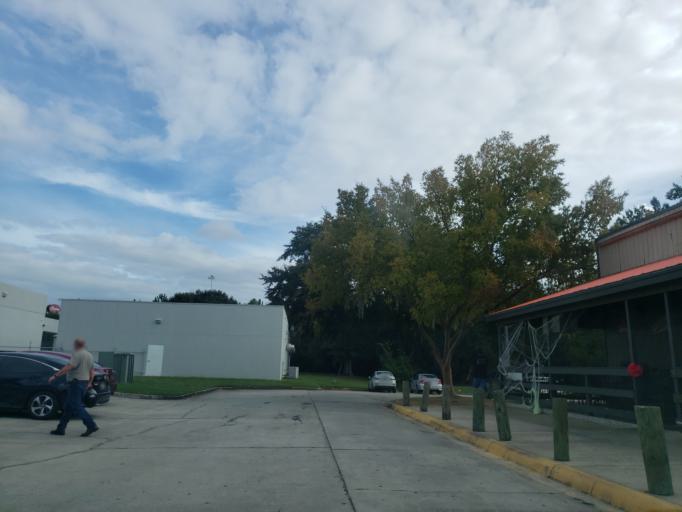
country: US
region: Georgia
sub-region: Chatham County
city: Georgetown
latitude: 32.0069
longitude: -81.2847
